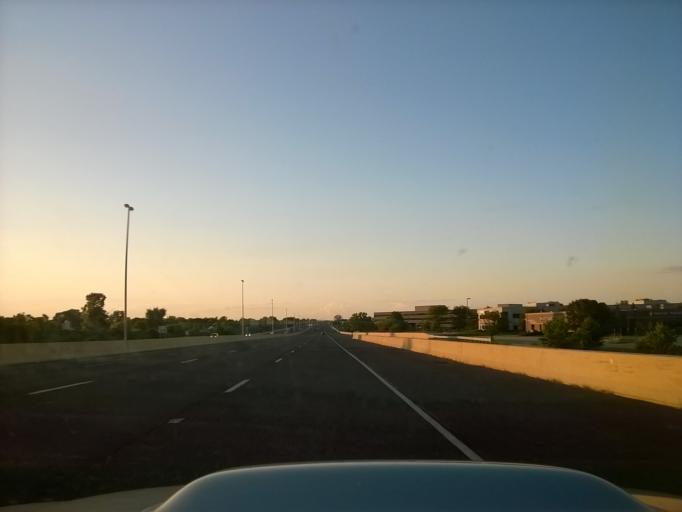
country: US
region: Indiana
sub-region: Boone County
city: Zionsville
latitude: 39.8839
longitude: -86.2690
